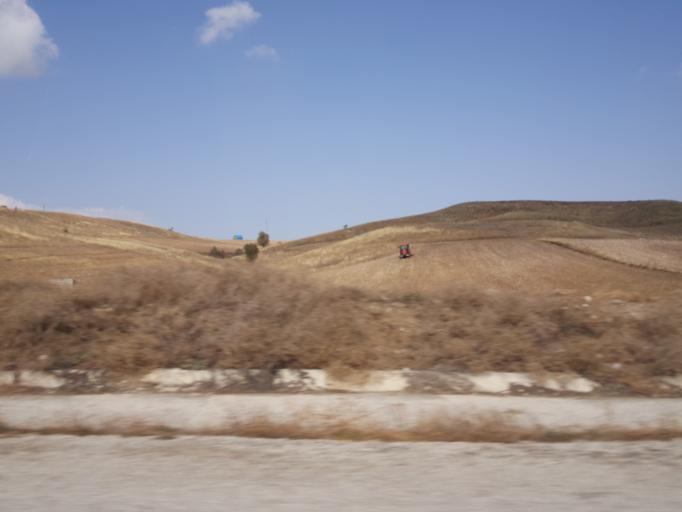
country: TR
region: Corum
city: Alaca
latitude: 40.1570
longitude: 34.6944
